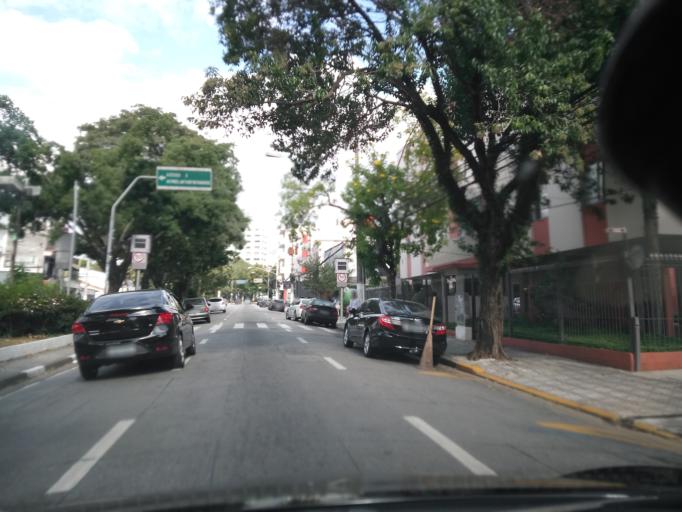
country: BR
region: Sao Paulo
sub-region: Sao Bernardo Do Campo
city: Sao Bernardo do Campo
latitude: -23.6682
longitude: -46.5681
